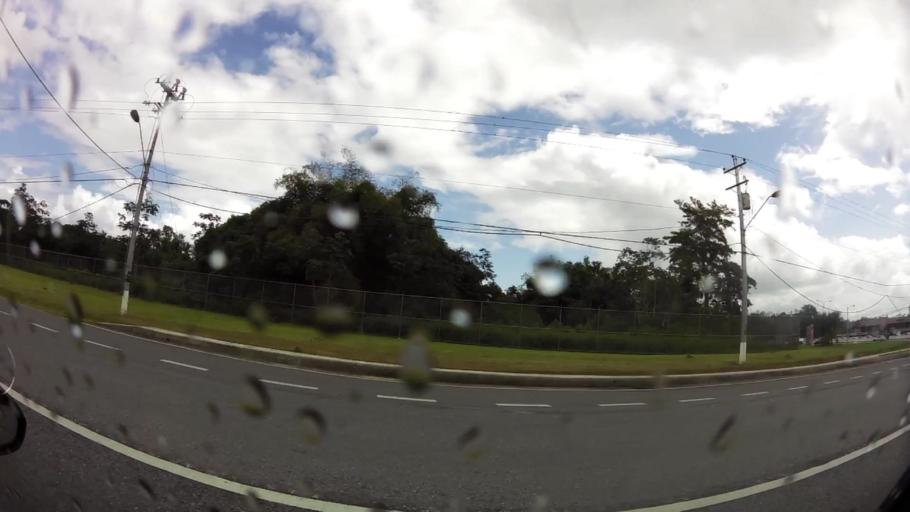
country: TT
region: Tunapuna/Piarco
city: Arouca
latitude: 10.6167
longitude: -61.3436
